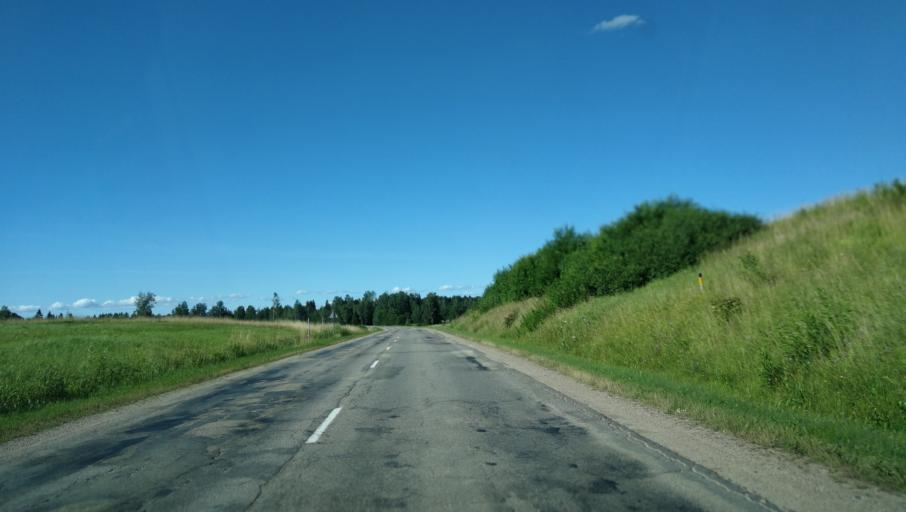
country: LV
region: Madonas Rajons
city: Madona
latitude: 56.9651
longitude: 26.0477
